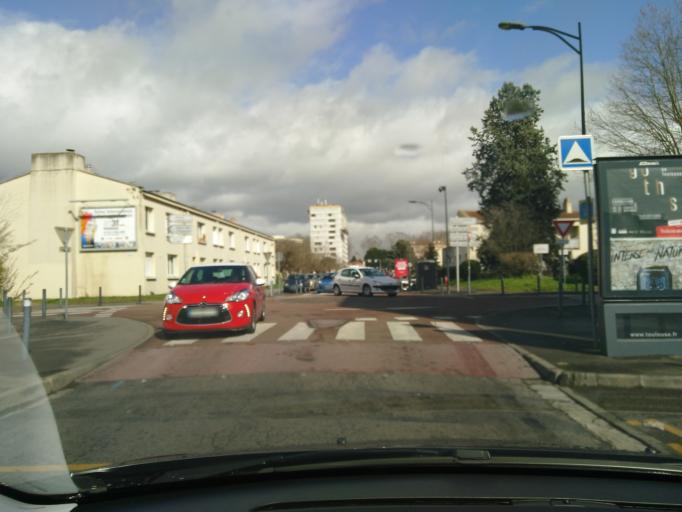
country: FR
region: Midi-Pyrenees
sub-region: Departement de la Haute-Garonne
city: Toulouse
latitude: 43.5796
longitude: 1.4597
